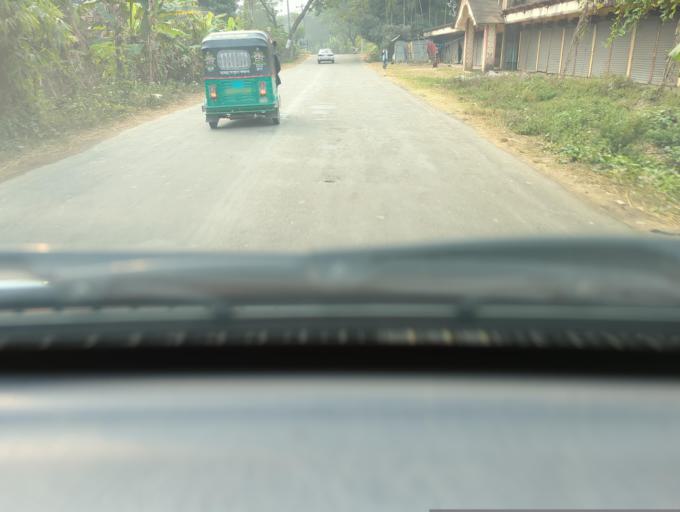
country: BD
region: Sylhet
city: Maulavi Bazar
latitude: 24.5257
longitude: 91.7327
